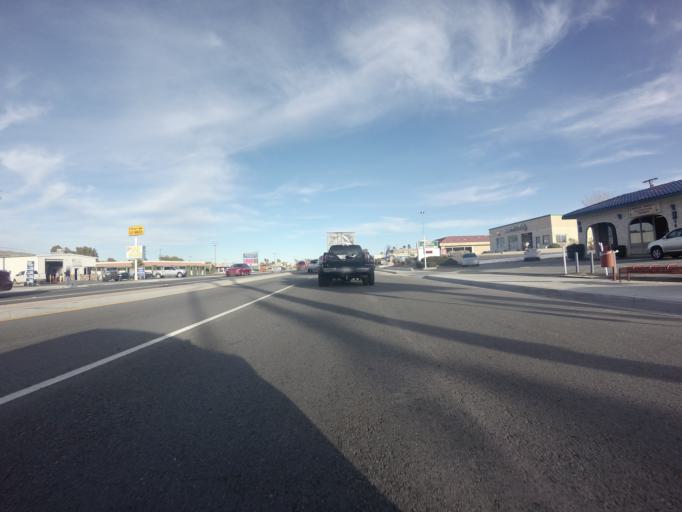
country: US
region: California
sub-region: San Bernardino County
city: Yucca Valley
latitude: 34.1206
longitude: -116.4352
